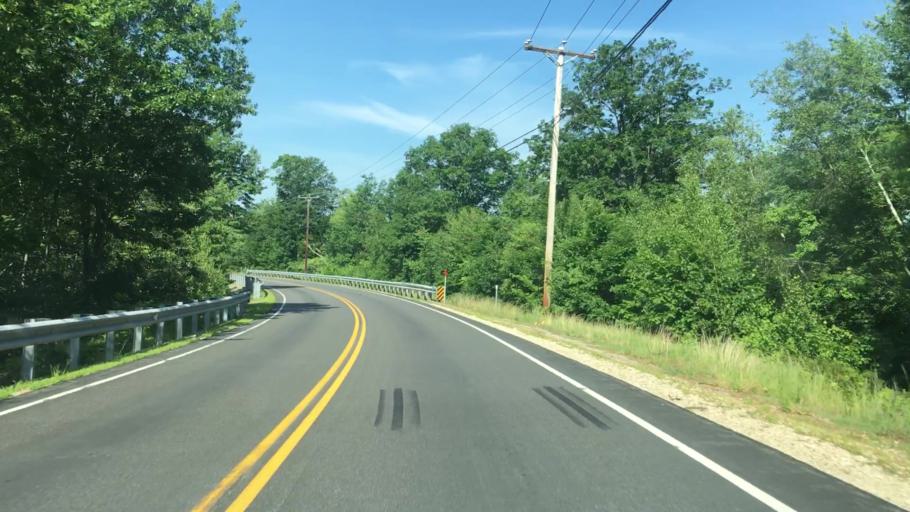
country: US
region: New Hampshire
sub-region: Merrimack County
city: Contoocook
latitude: 43.1939
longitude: -71.7360
